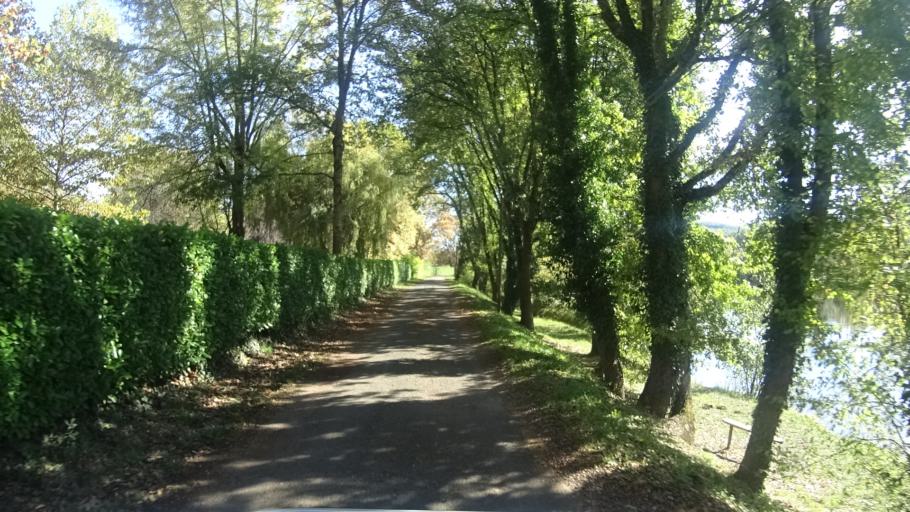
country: FR
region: Aquitaine
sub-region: Departement de la Dordogne
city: Saint-Cyprien
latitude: 44.8520
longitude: 1.0475
